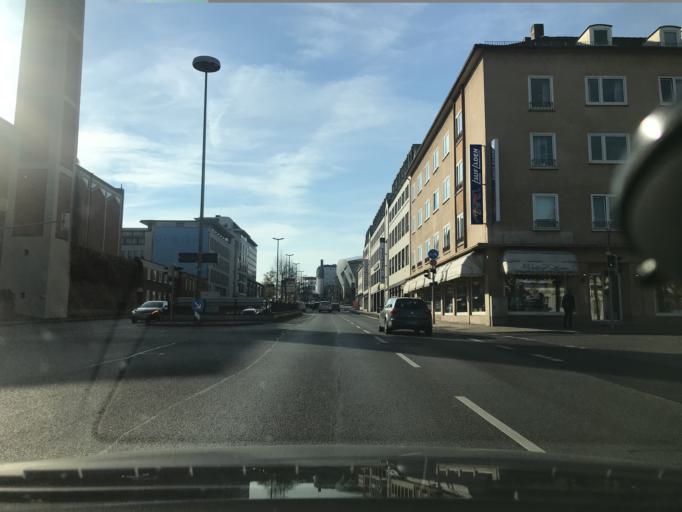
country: DE
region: Hesse
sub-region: Regierungsbezirk Kassel
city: Kassel
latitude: 51.3126
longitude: 9.4967
